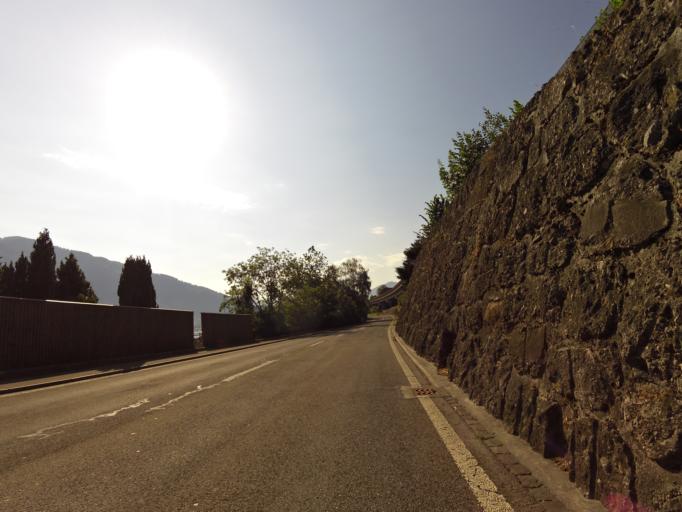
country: CH
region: Schwyz
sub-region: Bezirk Schwyz
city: Arth
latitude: 47.0716
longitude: 8.5002
